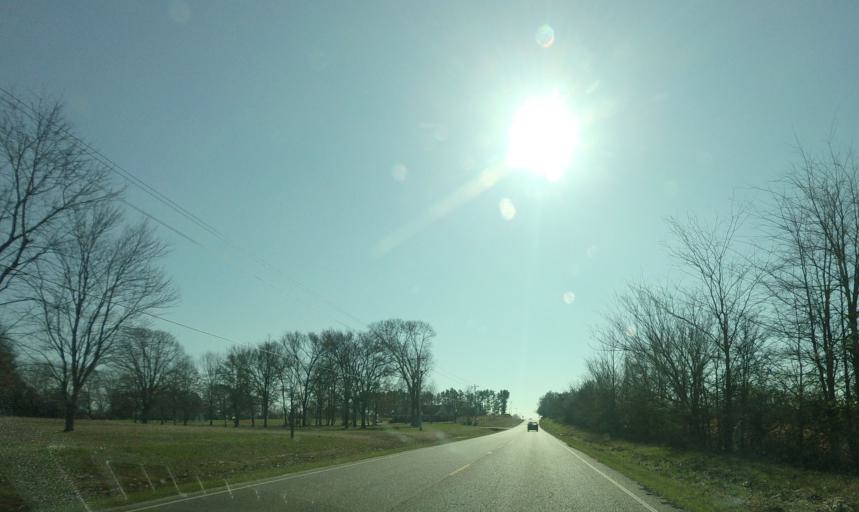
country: US
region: Tennessee
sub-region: Shelby County
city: Collierville
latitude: 34.9727
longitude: -89.6889
